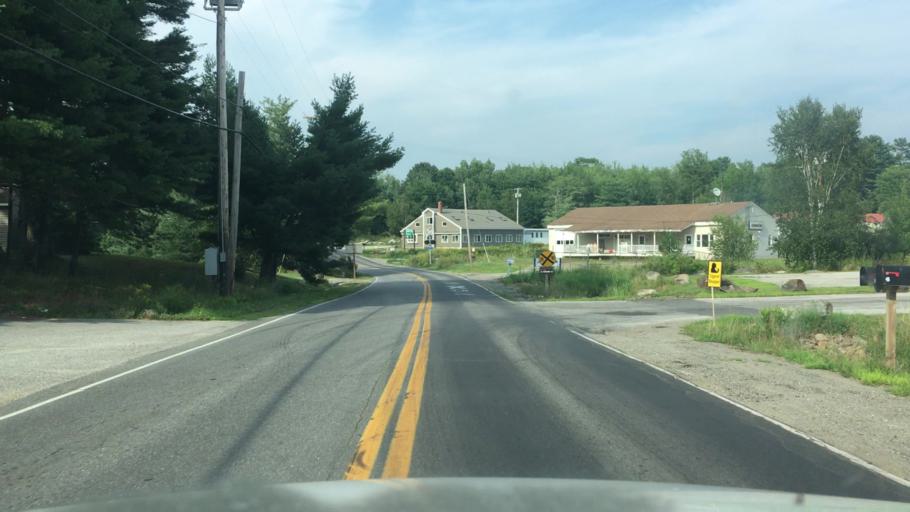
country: US
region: Maine
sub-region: Lincoln County
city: Waldoboro
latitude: 44.1041
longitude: -69.3683
